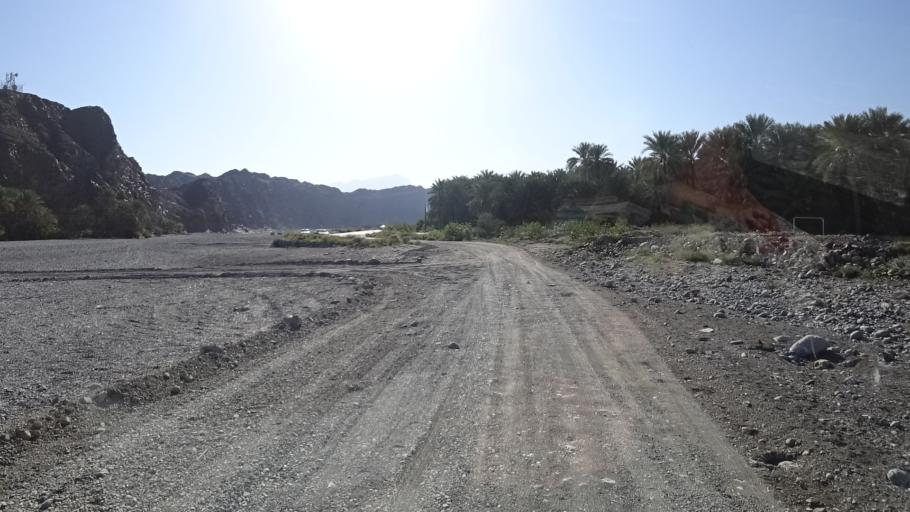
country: OM
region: Al Batinah
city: Bayt al `Awabi
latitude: 23.3856
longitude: 57.6599
